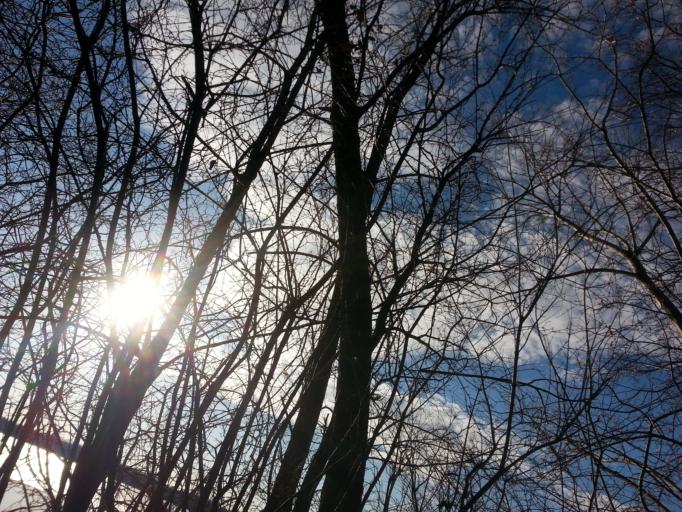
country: US
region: Minnesota
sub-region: Hennepin County
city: Richfield
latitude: 44.9227
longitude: -93.2970
